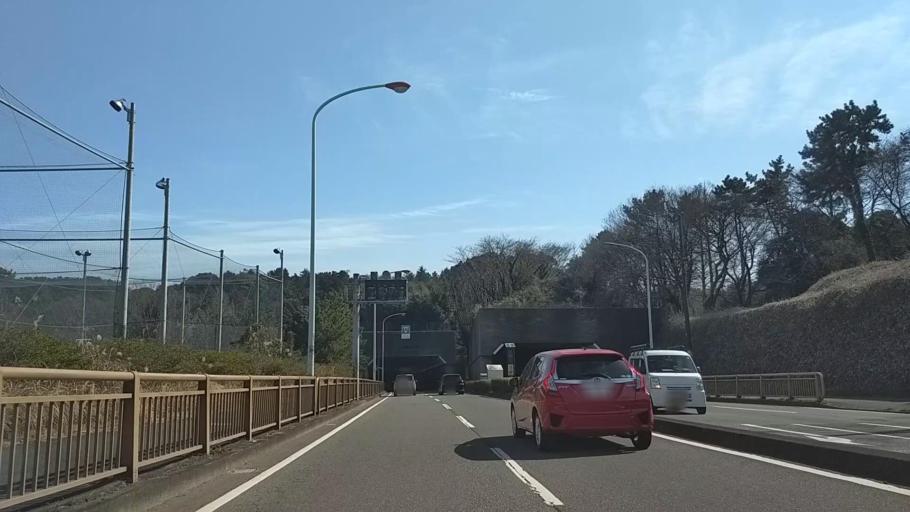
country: JP
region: Kanagawa
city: Fujisawa
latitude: 35.3528
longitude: 139.4441
